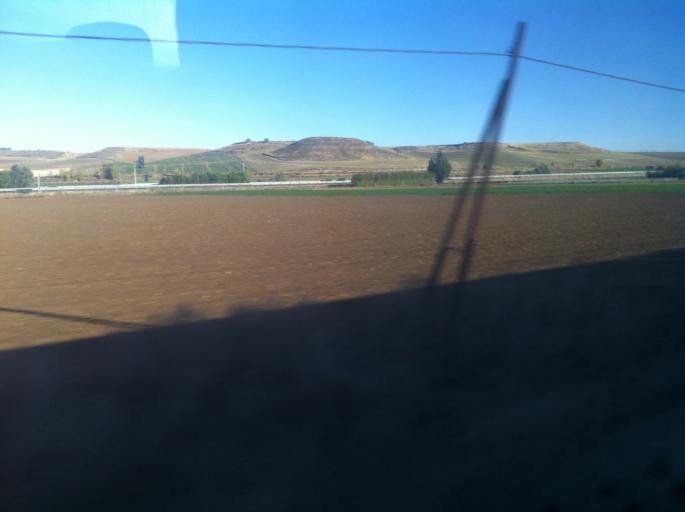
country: ES
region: Castille and Leon
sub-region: Provincia de Palencia
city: Reinoso de Cerrato
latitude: 41.9906
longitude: -4.3999
